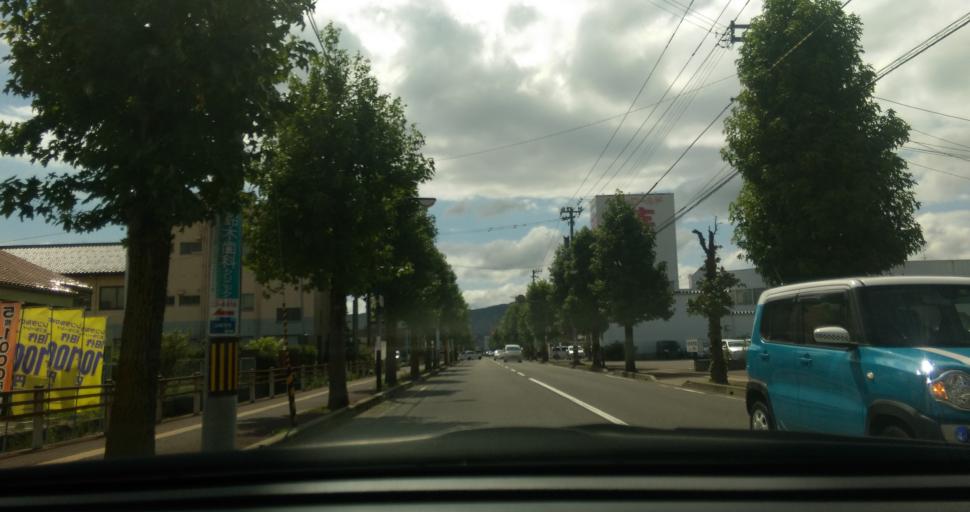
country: JP
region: Fukui
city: Fukui-shi
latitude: 36.0879
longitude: 136.2183
